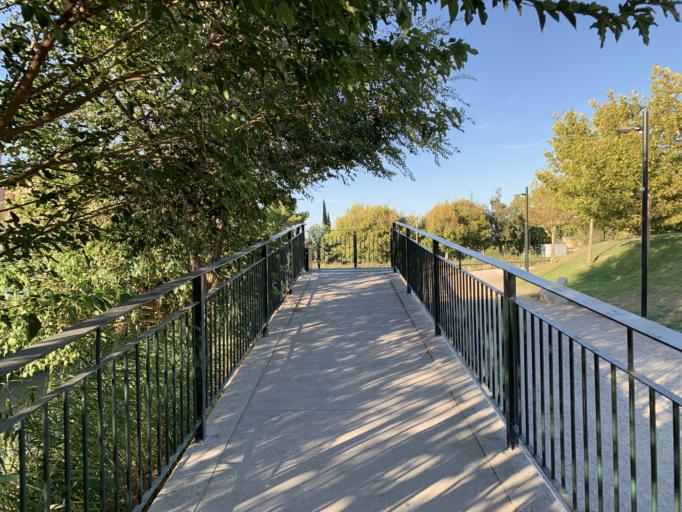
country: ES
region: Aragon
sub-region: Provincia de Zaragoza
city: Zaragoza
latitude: 41.6304
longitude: -0.8762
